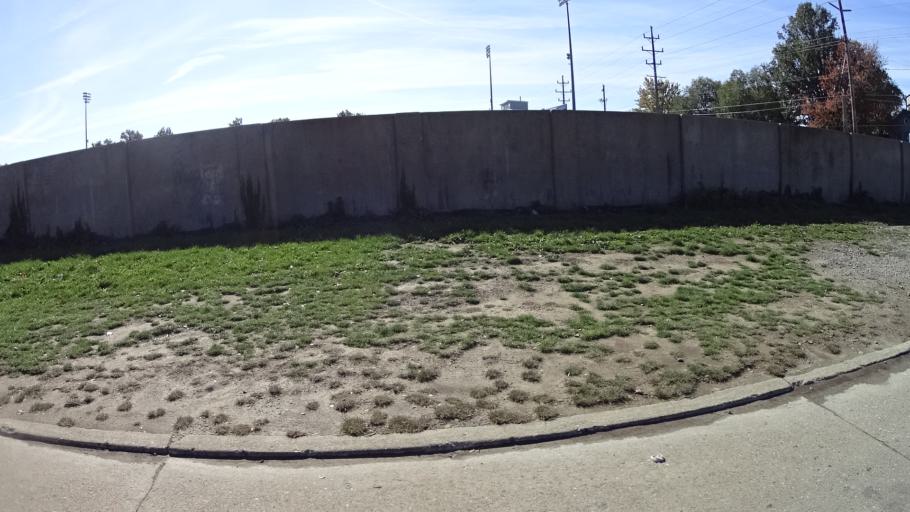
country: US
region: Ohio
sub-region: Lorain County
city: Lorain
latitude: 41.4477
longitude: -82.1848
